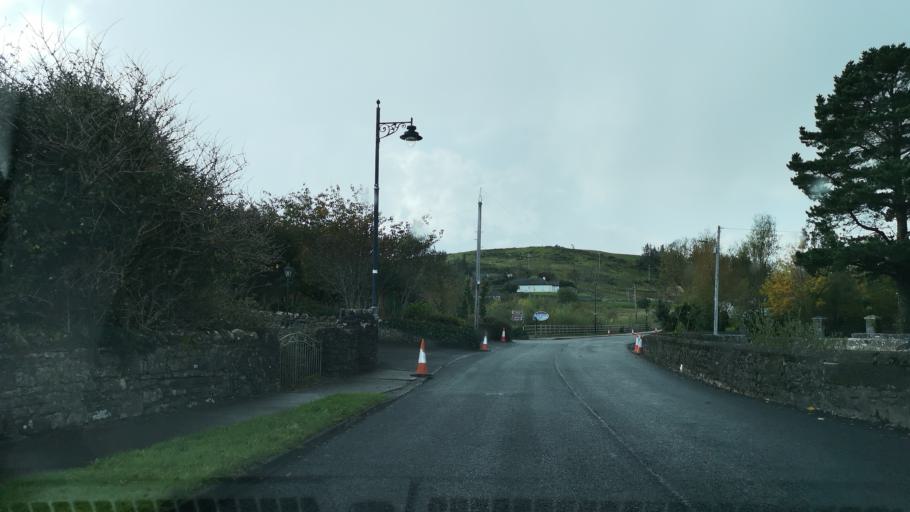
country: IE
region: Connaught
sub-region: Maigh Eo
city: Westport
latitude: 53.7970
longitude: -9.5533
